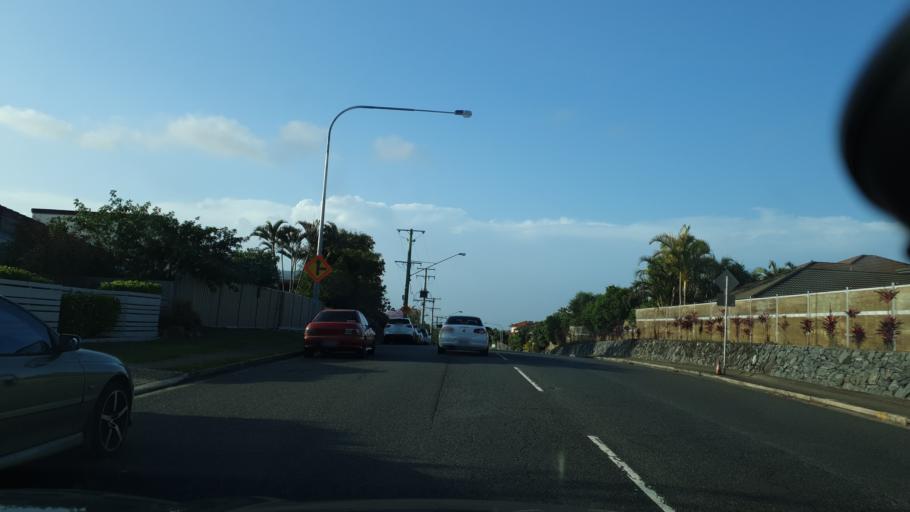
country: AU
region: Queensland
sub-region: Brisbane
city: Belmont
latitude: -27.4906
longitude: 153.1277
